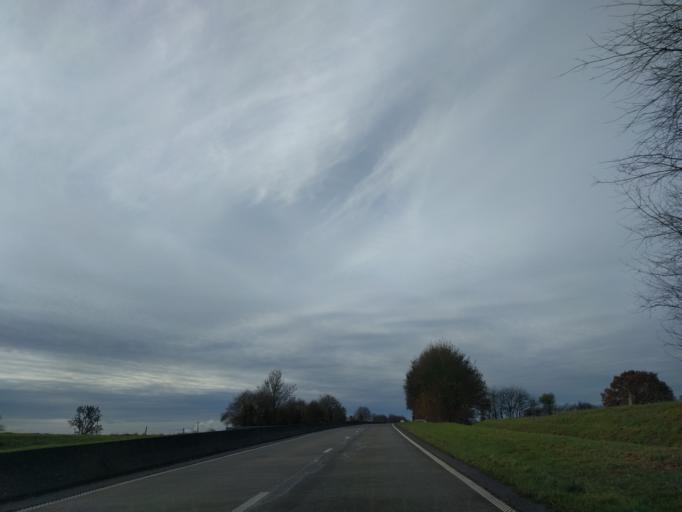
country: BE
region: Wallonia
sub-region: Province de Namur
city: Houyet
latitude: 50.2451
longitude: 5.0025
